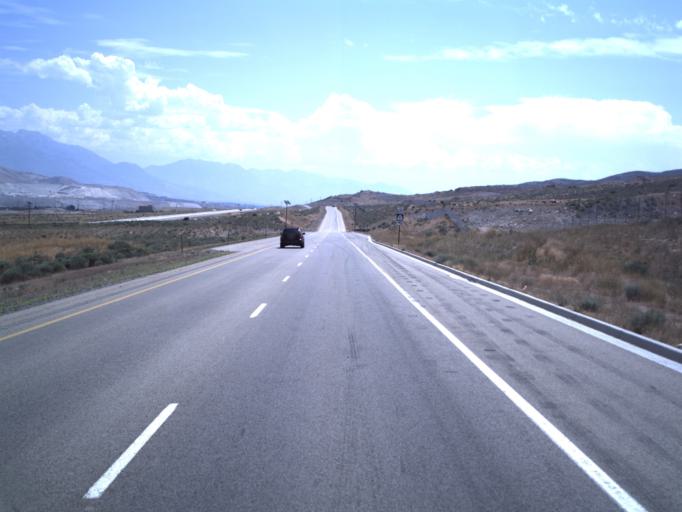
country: US
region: Utah
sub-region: Salt Lake County
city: Herriman
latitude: 40.4828
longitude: -111.9911
